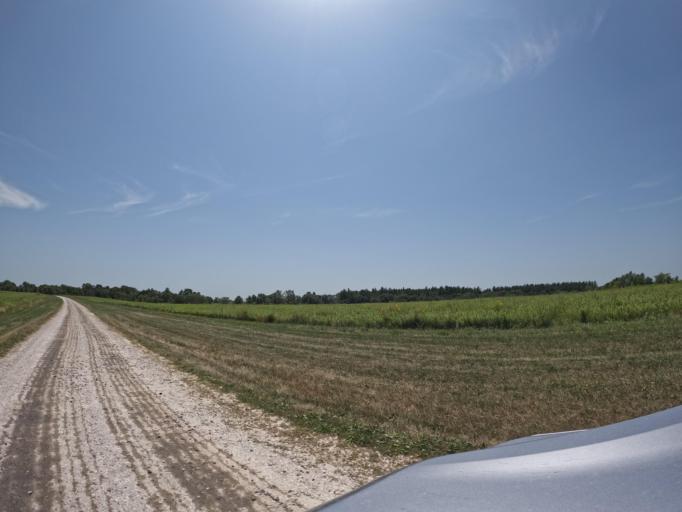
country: US
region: Iowa
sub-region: Henry County
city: Mount Pleasant
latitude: 40.9408
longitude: -91.5866
